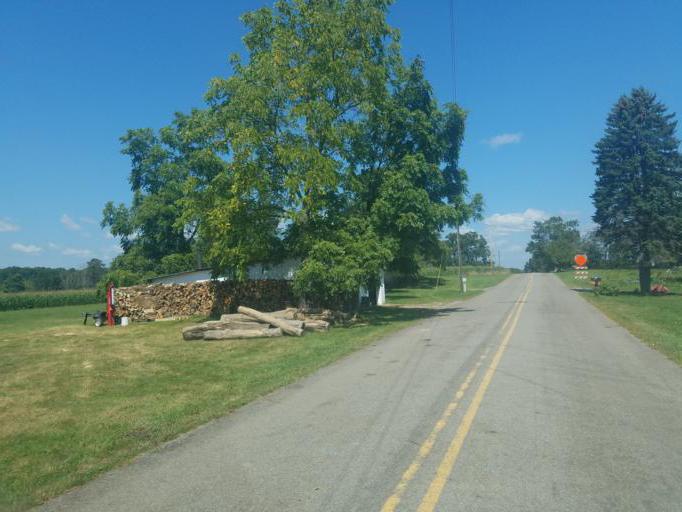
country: US
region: Pennsylvania
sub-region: Clarion County
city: Knox
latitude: 41.1961
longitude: -79.4921
